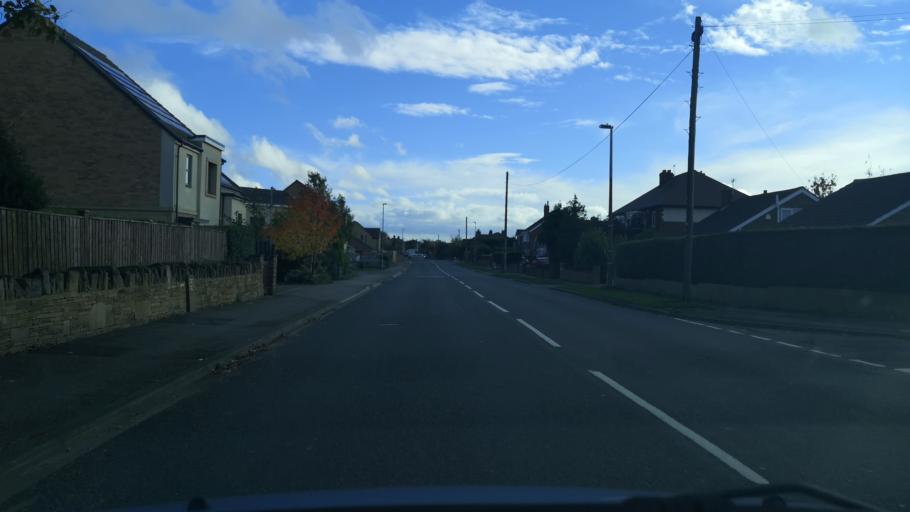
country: GB
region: England
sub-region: Kirklees
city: Heckmondwike
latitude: 53.7182
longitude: -1.6633
